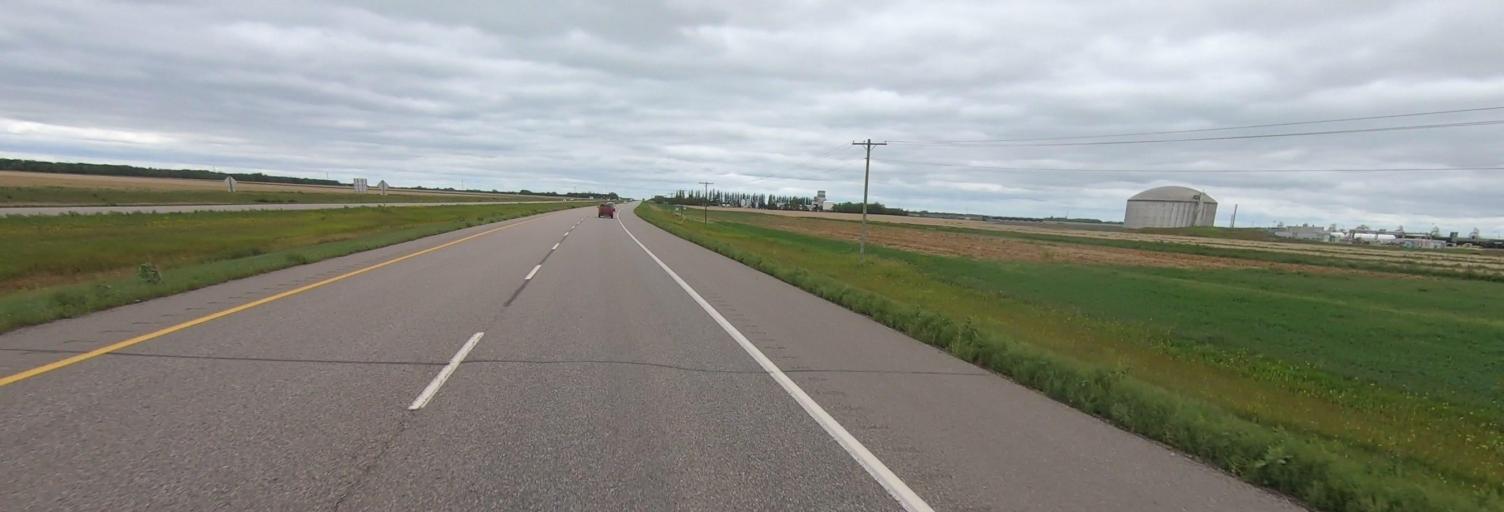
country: CA
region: Manitoba
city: Portage la Prairie
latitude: 49.9753
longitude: -98.4975
